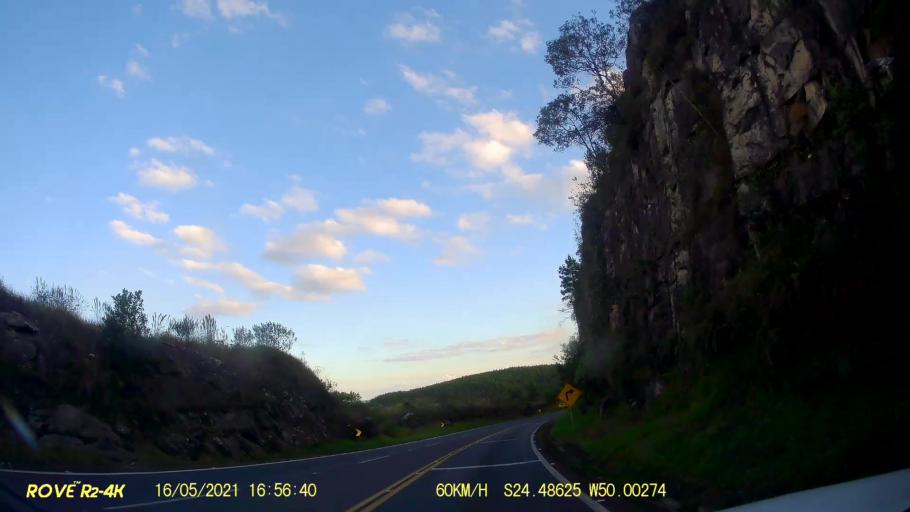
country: BR
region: Parana
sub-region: Pirai Do Sul
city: Pirai do Sul
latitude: -24.4864
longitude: -50.0027
